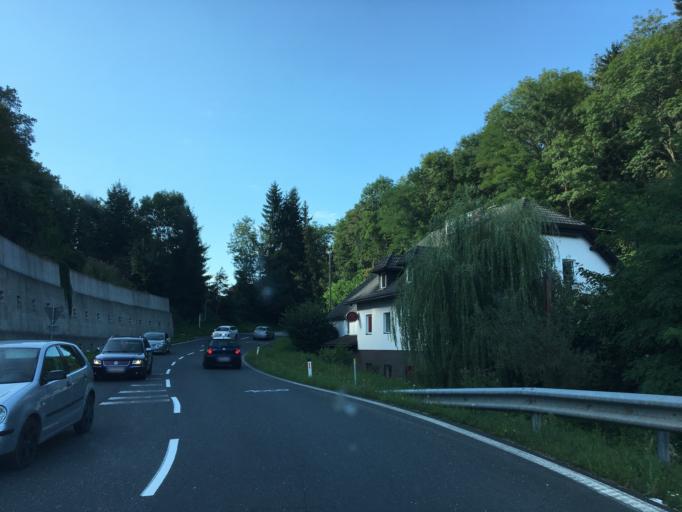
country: AT
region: Carinthia
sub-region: Politischer Bezirk Volkermarkt
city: Voelkermarkt
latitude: 46.6562
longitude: 14.6330
